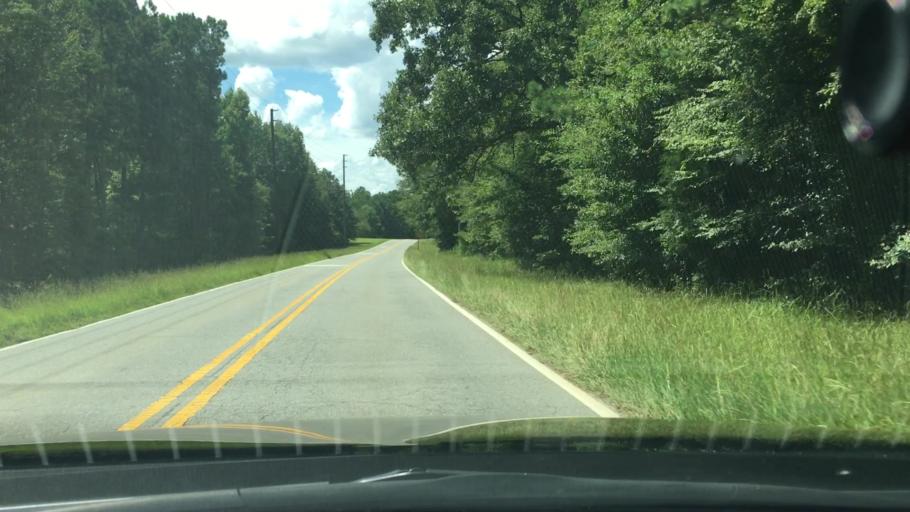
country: US
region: Georgia
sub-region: Putnam County
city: Jefferson
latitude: 33.3579
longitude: -83.2604
